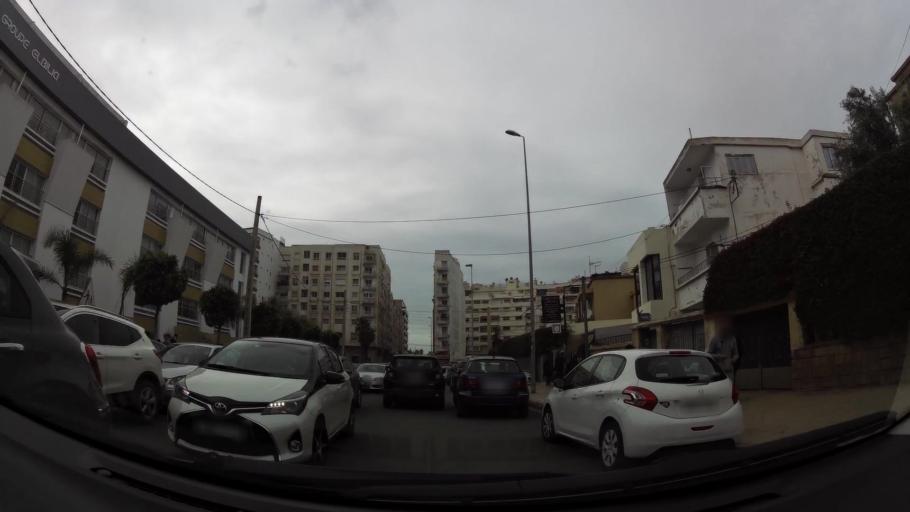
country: MA
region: Grand Casablanca
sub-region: Casablanca
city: Casablanca
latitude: 33.5945
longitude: -7.6504
